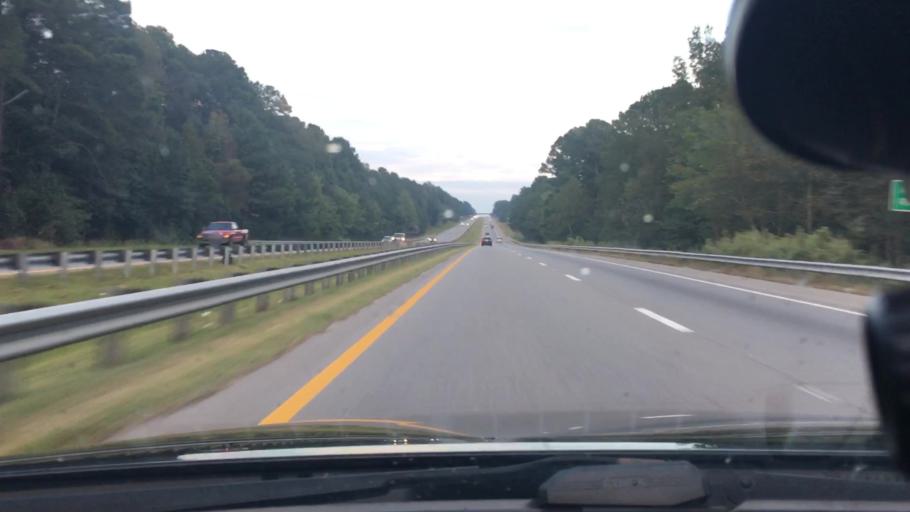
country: US
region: North Carolina
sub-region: Wake County
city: Holly Springs
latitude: 35.6750
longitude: -78.9161
